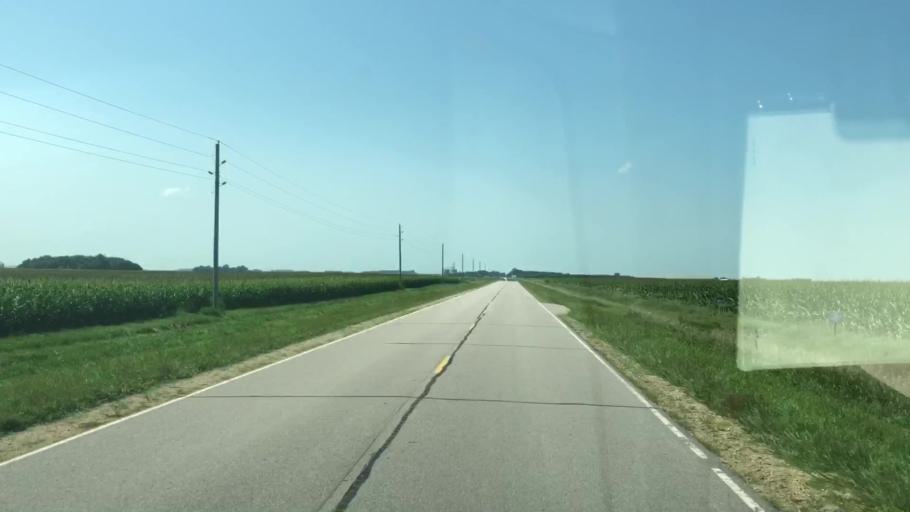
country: US
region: Iowa
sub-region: O'Brien County
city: Sheldon
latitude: 43.2443
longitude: -95.7898
